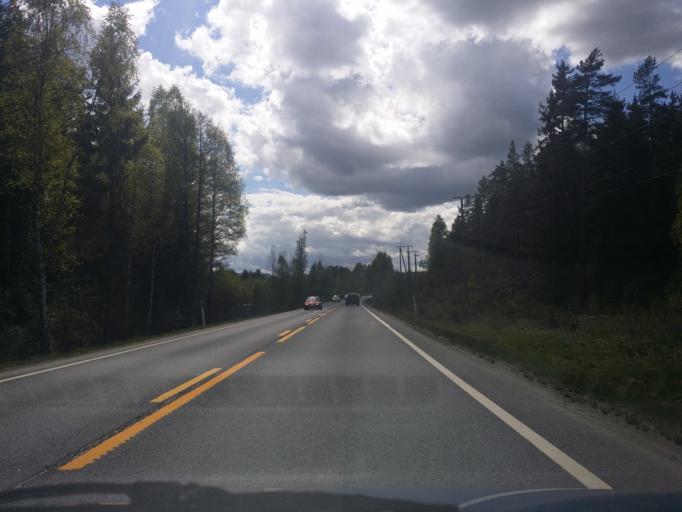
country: NO
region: Buskerud
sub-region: Modum
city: Vikersund
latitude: 59.9536
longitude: 9.9750
